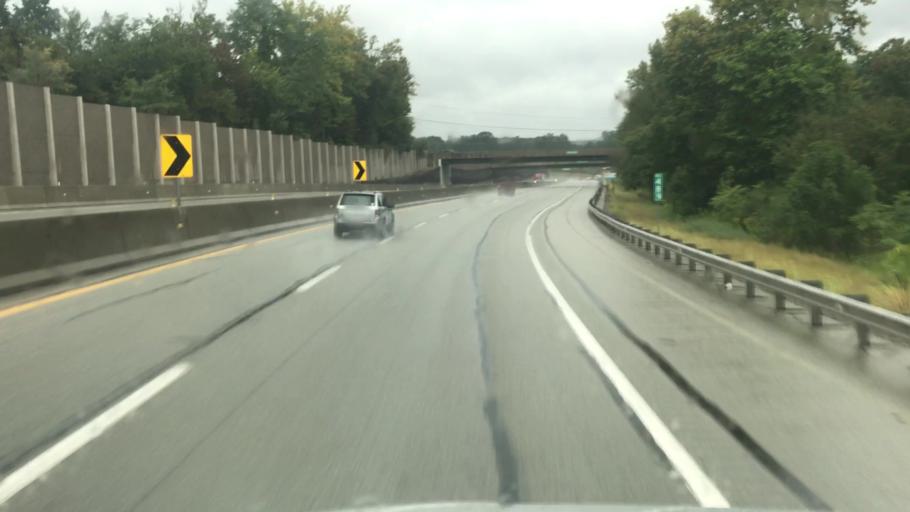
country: US
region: Pennsylvania
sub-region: Allegheny County
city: Oakmont
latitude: 40.5246
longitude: -79.8198
